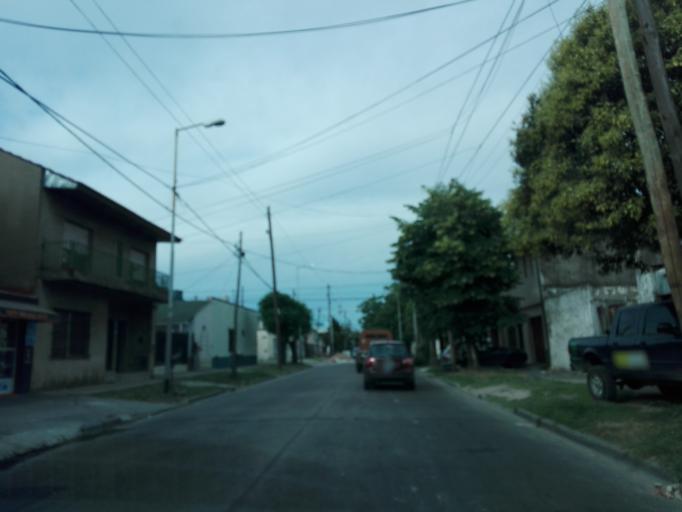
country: AR
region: Buenos Aires
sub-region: Partido de Avellaneda
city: Avellaneda
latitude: -34.6868
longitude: -58.3490
